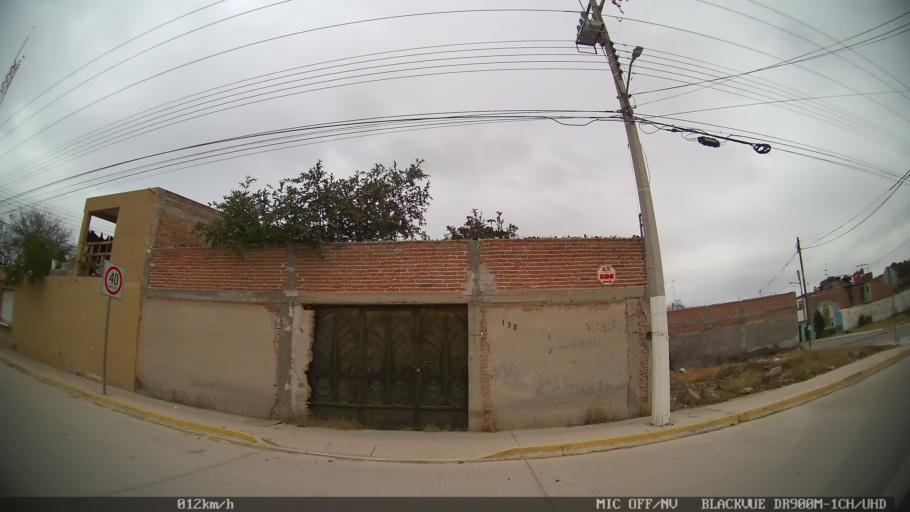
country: MX
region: San Luis Potosi
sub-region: Soledad de Graciano Sanchez
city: Soledad de Graciano Sanchez
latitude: 22.1603
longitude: -100.9248
